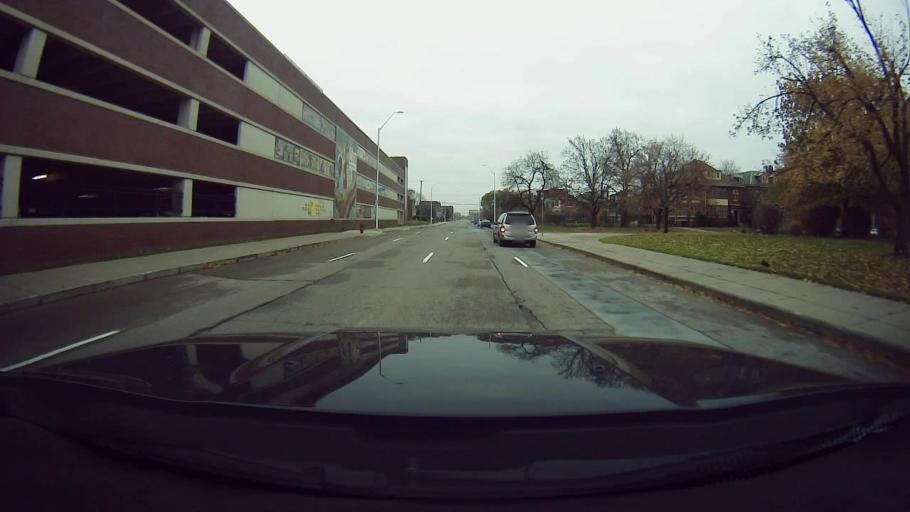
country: US
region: Michigan
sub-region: Wayne County
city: Hamtramck
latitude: 42.3615
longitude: -83.0617
